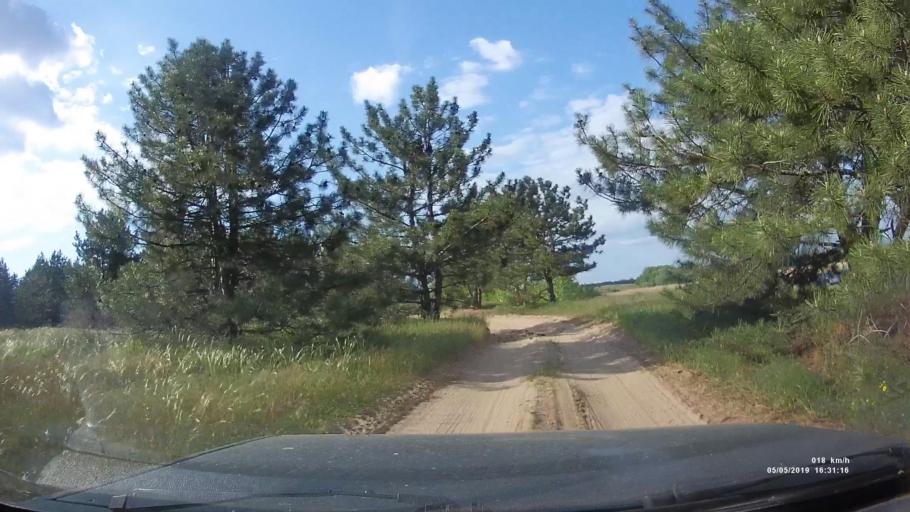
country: RU
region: Rostov
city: Ust'-Donetskiy
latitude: 47.7758
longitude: 41.0150
